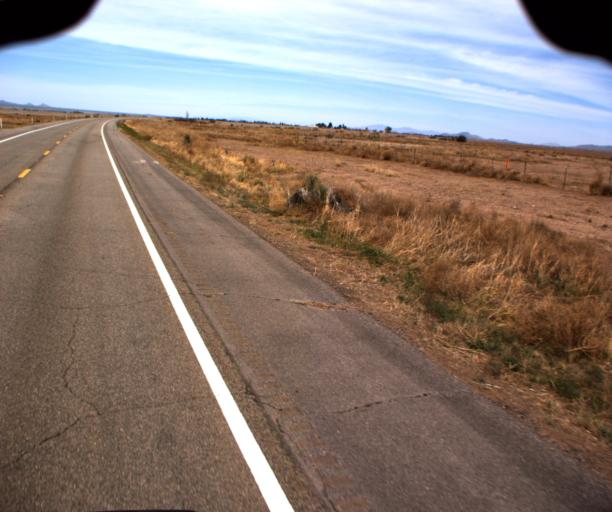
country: US
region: Arizona
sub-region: Cochise County
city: Pirtleville
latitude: 31.5558
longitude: -109.6649
